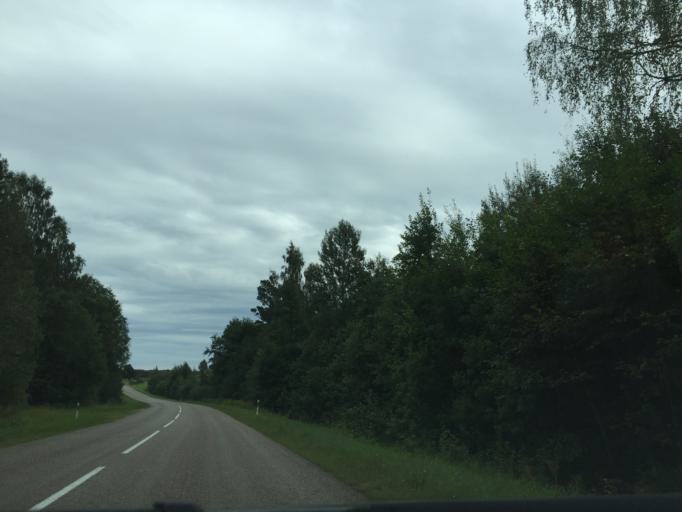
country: LV
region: Dagda
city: Dagda
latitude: 56.1839
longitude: 27.3759
